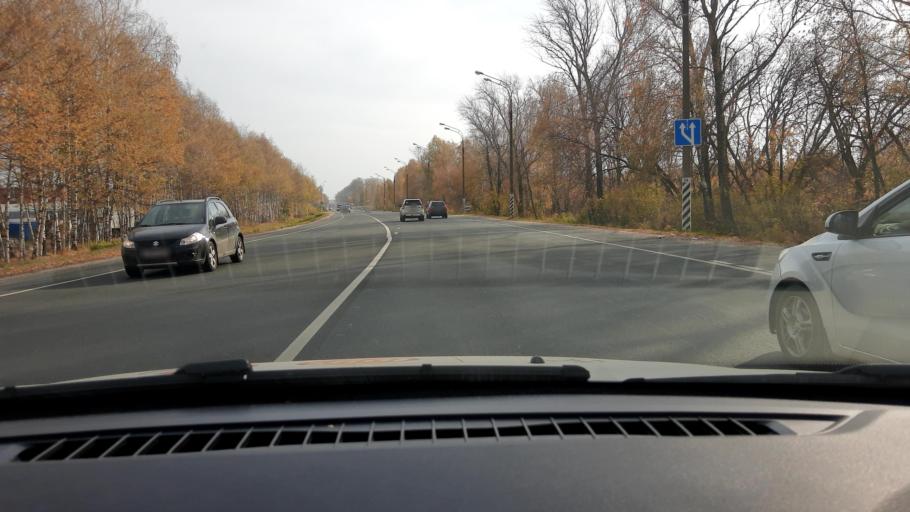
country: RU
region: Nizjnij Novgorod
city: Kstovo
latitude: 56.1456
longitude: 44.2174
